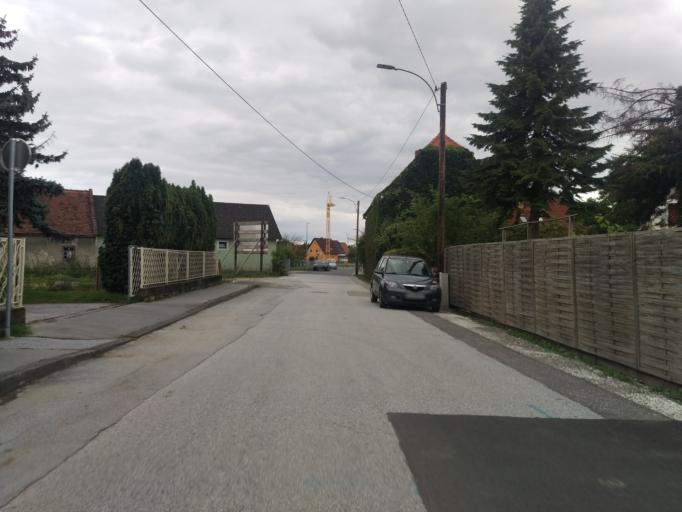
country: AT
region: Styria
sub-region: Politischer Bezirk Graz-Umgebung
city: Feldkirchen bei Graz
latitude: 47.0358
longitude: 15.4569
